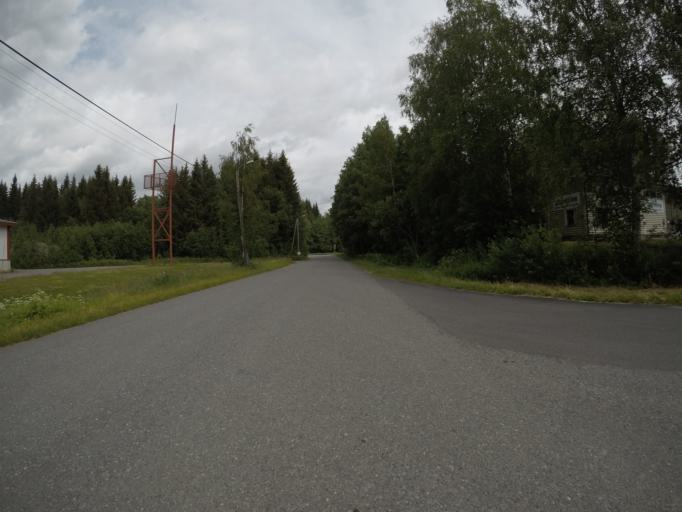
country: FI
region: Haeme
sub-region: Haemeenlinna
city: Haemeenlinna
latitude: 60.9676
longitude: 24.4380
